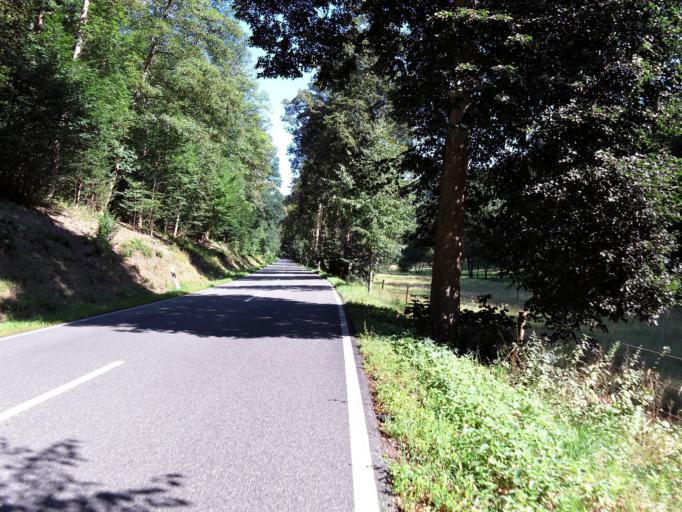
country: DE
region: Rheinland-Pfalz
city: Frankeneck
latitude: 49.3717
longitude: 8.0262
